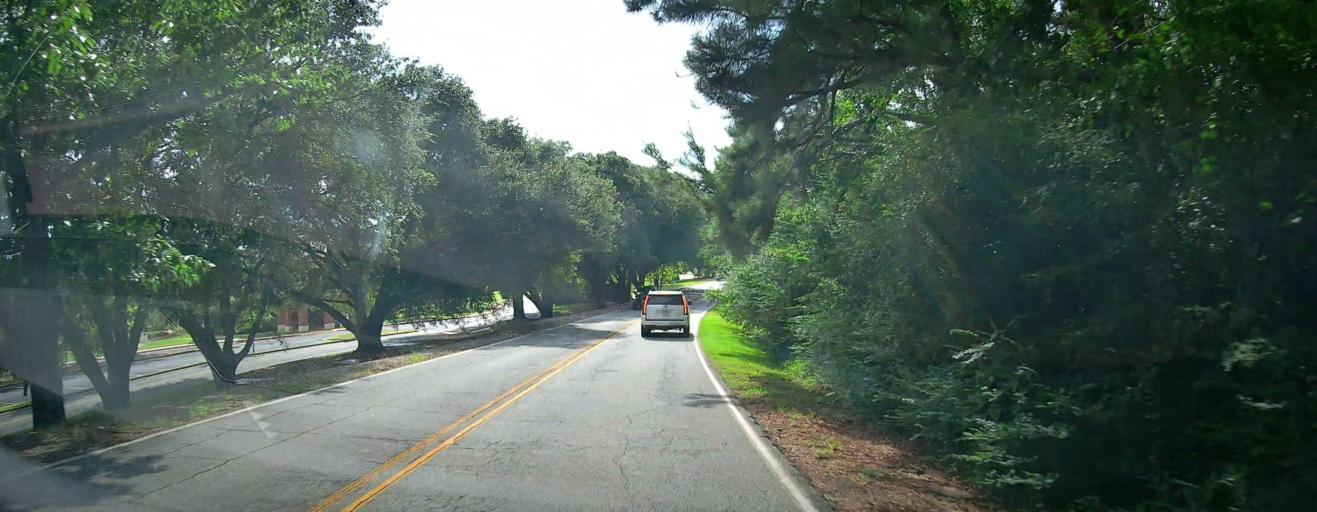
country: US
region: Alabama
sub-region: Russell County
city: Phenix City
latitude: 32.5296
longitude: -84.9867
